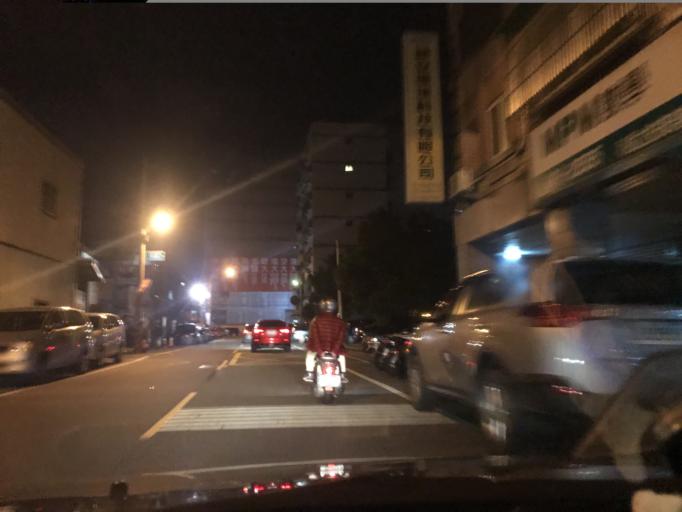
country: TW
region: Taiwan
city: Taoyuan City
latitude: 24.9507
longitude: 121.2094
